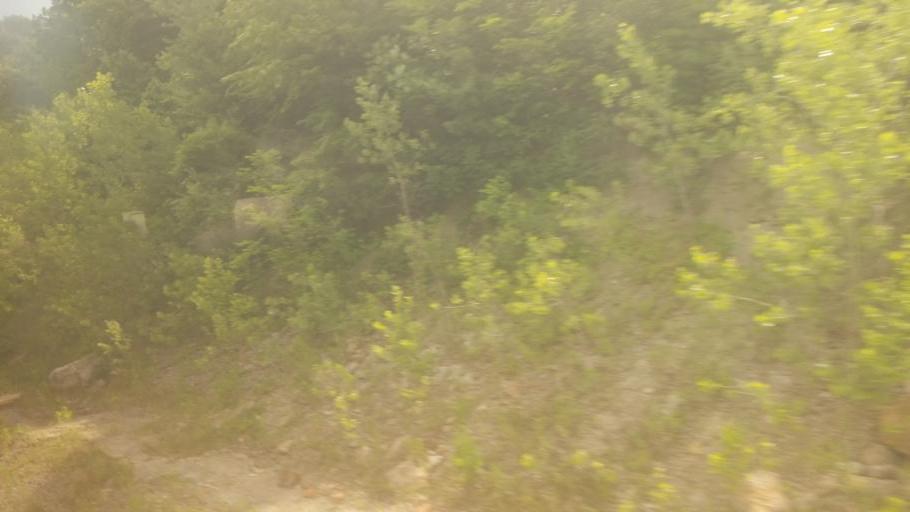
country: US
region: Missouri
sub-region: Jackson County
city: East Independence
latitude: 39.1649
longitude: -94.3594
